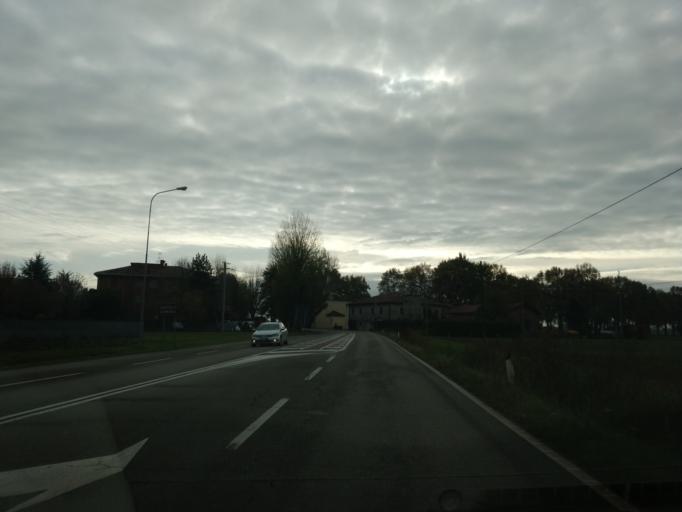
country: IT
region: Emilia-Romagna
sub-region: Provincia di Bologna
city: Castello d'Argile
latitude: 44.6677
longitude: 11.3049
